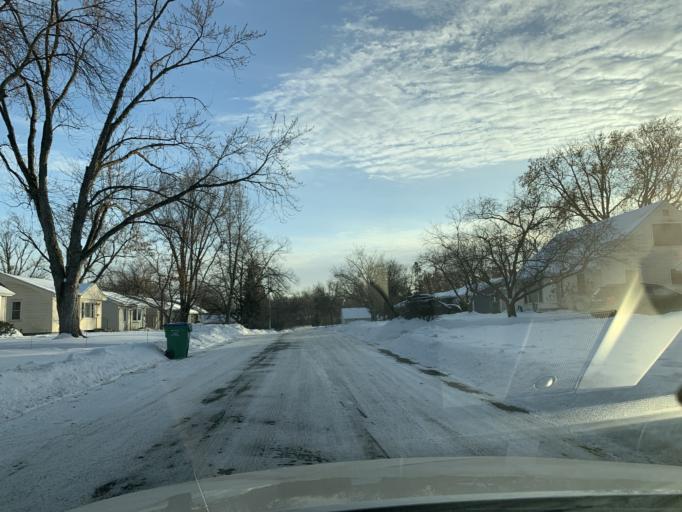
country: US
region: Minnesota
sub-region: Hennepin County
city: Minnetonka Mills
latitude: 44.9495
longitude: -93.3983
